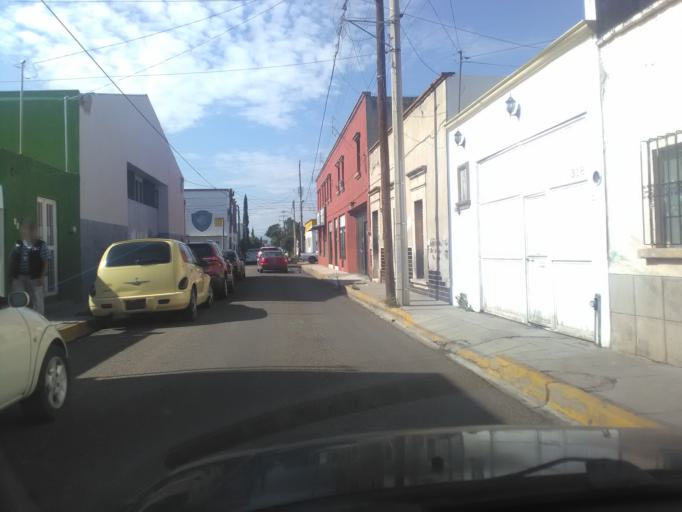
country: MX
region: Durango
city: Victoria de Durango
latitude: 24.0257
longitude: -104.6586
